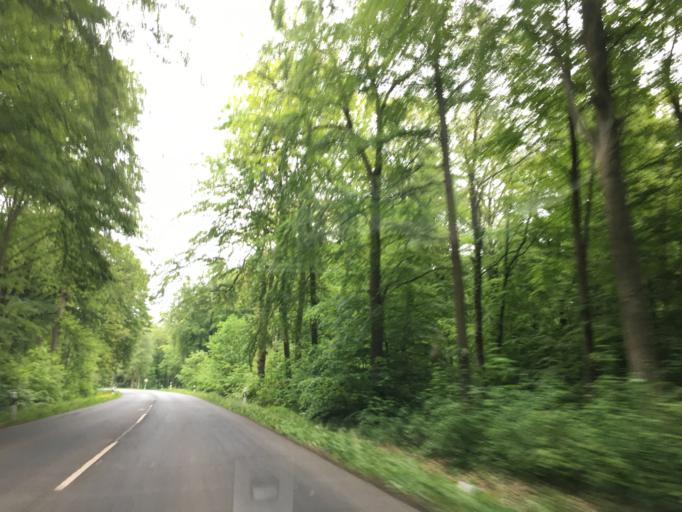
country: DE
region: Lower Saxony
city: Haste
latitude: 52.3794
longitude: 9.4063
